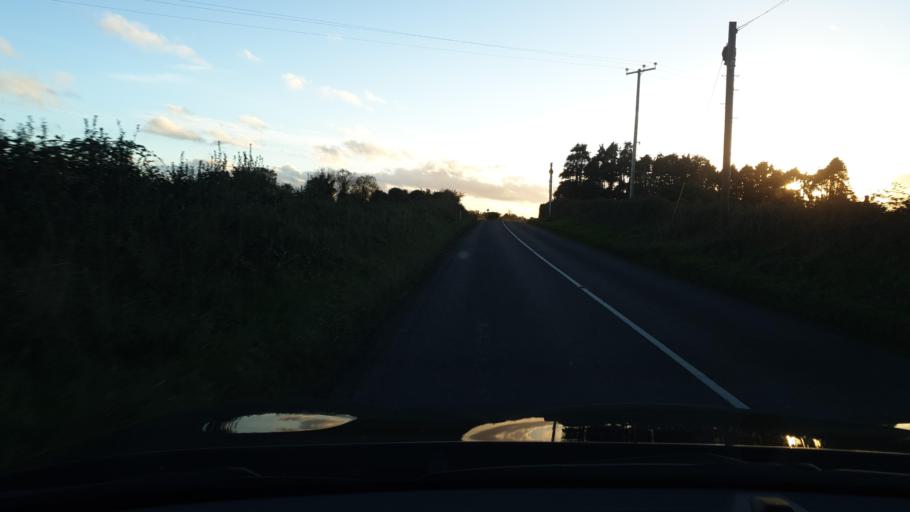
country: IE
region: Leinster
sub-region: Lu
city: Termonfeckin
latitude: 53.7522
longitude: -6.2830
